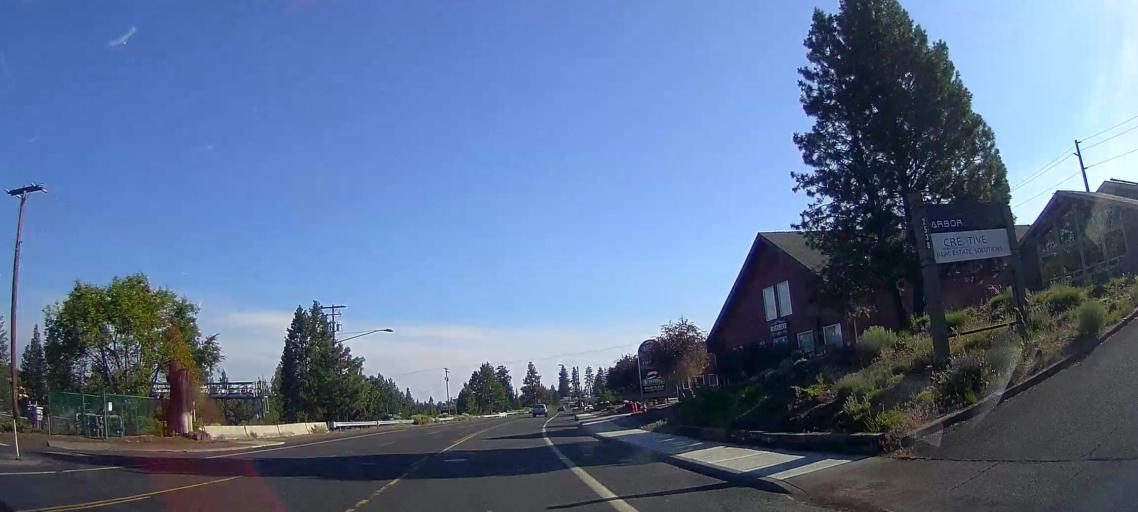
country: US
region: Oregon
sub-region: Deschutes County
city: Bend
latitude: 44.0752
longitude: -121.3056
